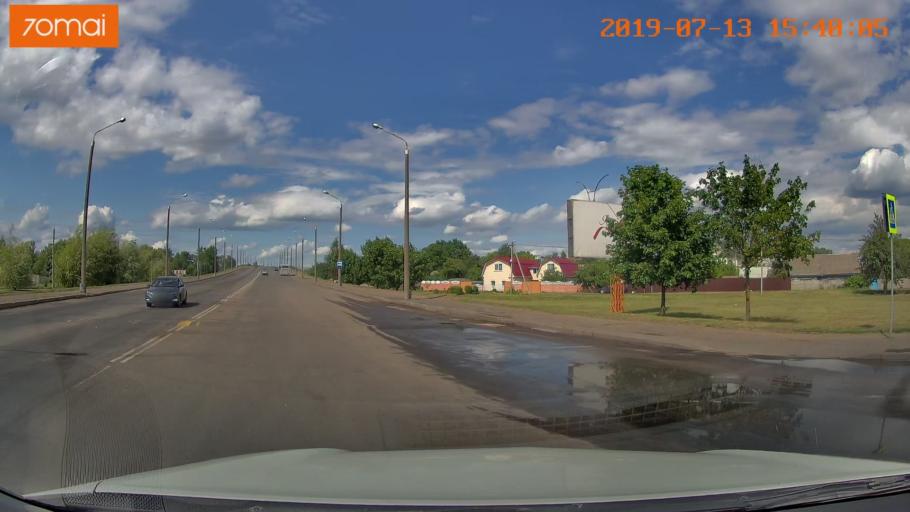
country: BY
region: Mogilev
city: Babruysk
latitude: 53.1353
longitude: 29.1888
